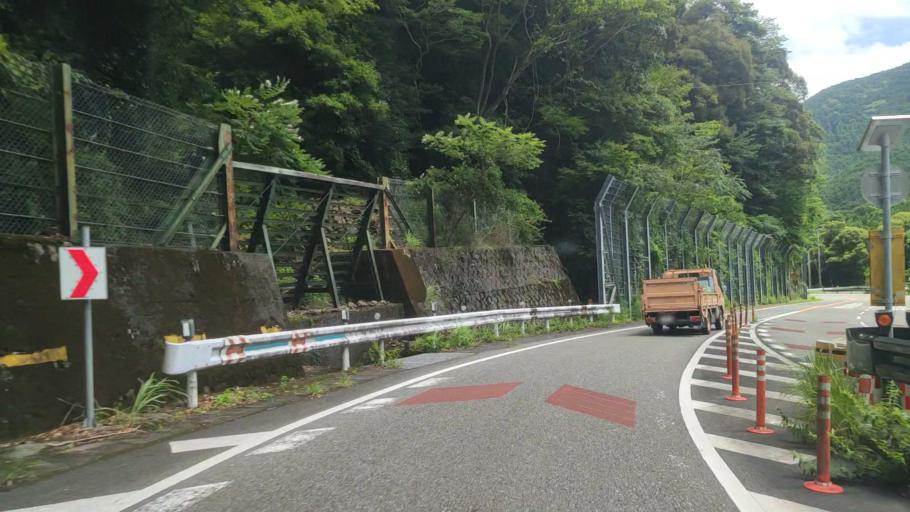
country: JP
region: Mie
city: Owase
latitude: 33.9218
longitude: 136.1011
